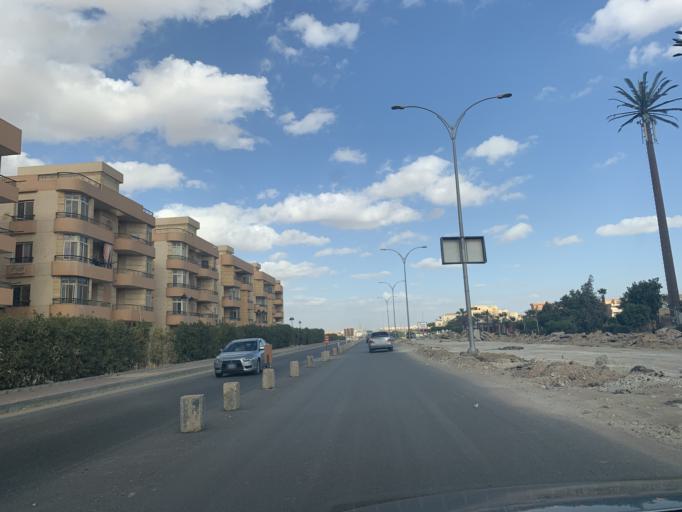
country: EG
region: Al Jizah
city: Madinat Sittah Uktubar
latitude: 29.9869
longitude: 30.9391
